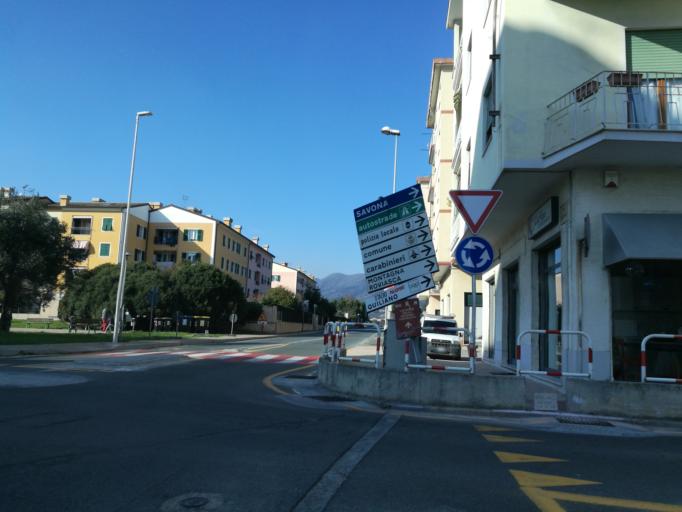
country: IT
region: Liguria
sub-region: Provincia di Savona
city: Valleggia
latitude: 44.2844
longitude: 8.4306
